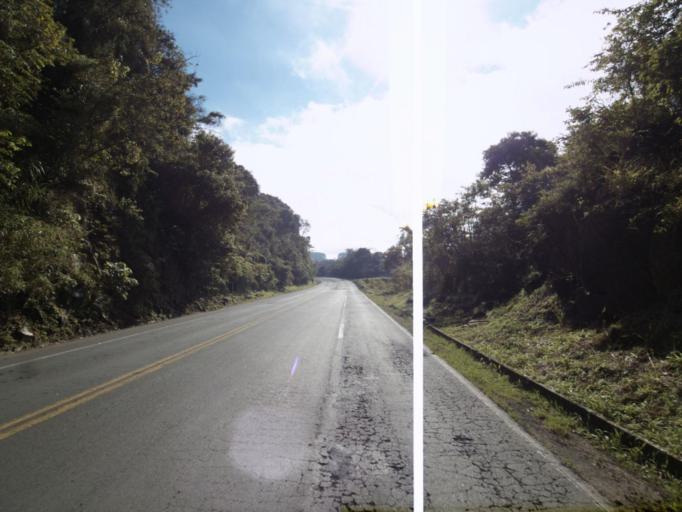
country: BR
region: Rio Grande do Sul
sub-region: Frederico Westphalen
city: Frederico Westphalen
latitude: -27.1295
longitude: -53.2126
